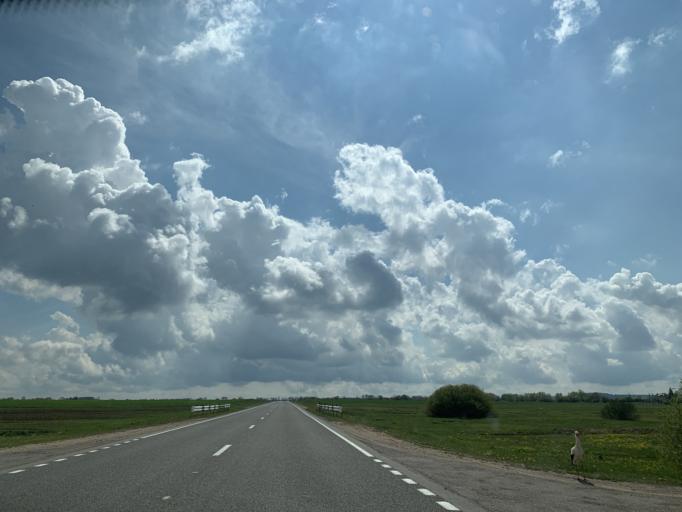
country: BY
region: Minsk
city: Nyasvizh
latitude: 53.2406
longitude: 26.7096
